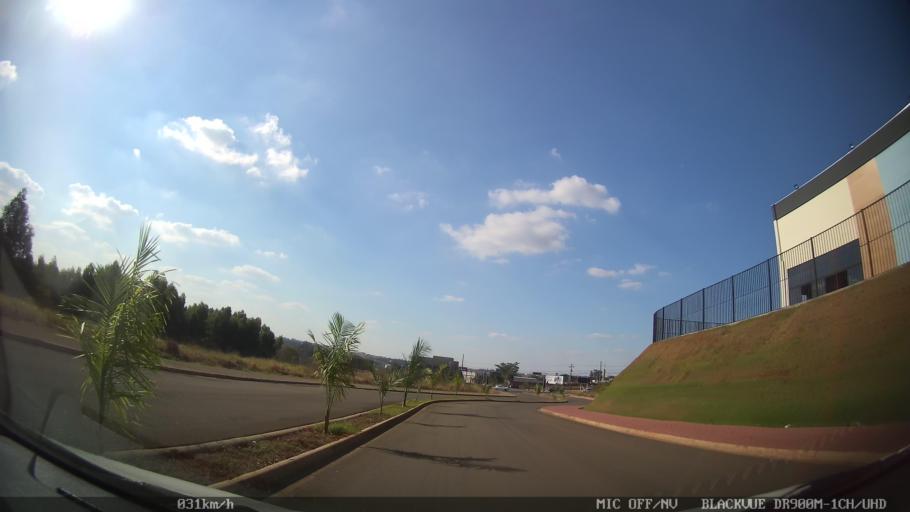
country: BR
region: Sao Paulo
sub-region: Nova Odessa
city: Nova Odessa
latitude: -22.7836
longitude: -47.3030
